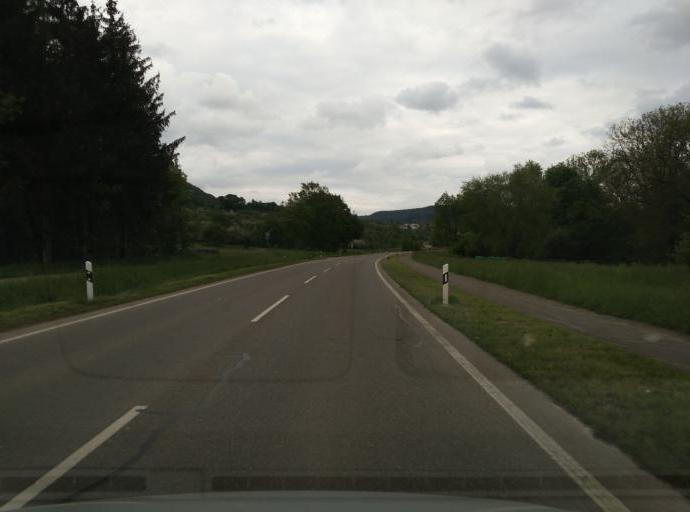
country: DE
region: Baden-Wuerttemberg
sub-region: Regierungsbezirk Stuttgart
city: Neuffen
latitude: 48.5705
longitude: 9.3747
